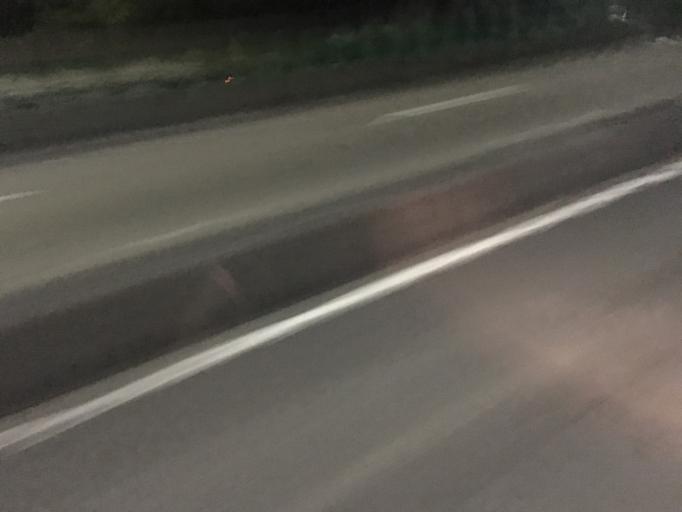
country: TW
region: Taiwan
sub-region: Hsinchu
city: Hsinchu
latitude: 24.7910
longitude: 120.9462
